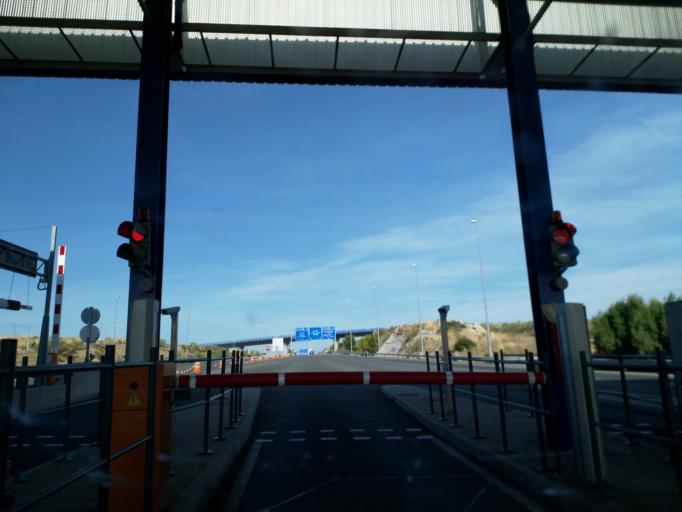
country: ES
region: Castille and Leon
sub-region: Provincia de Segovia
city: Villacastin
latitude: 40.7692
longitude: -4.4306
